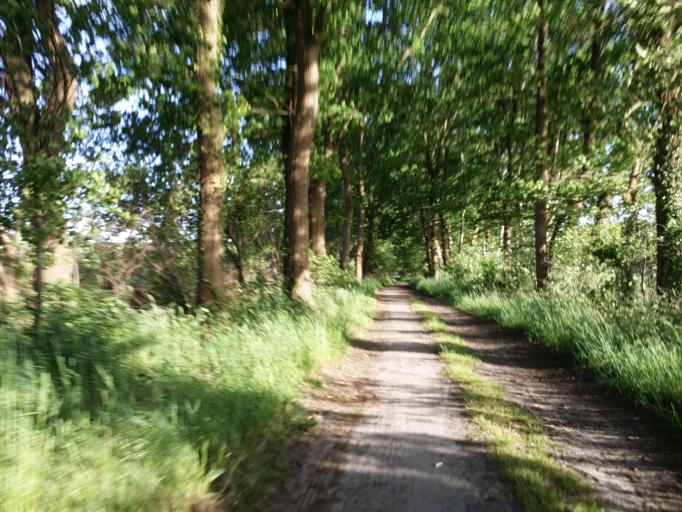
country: DE
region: Lower Saxony
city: Ganderkesee
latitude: 53.0140
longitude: 8.5519
